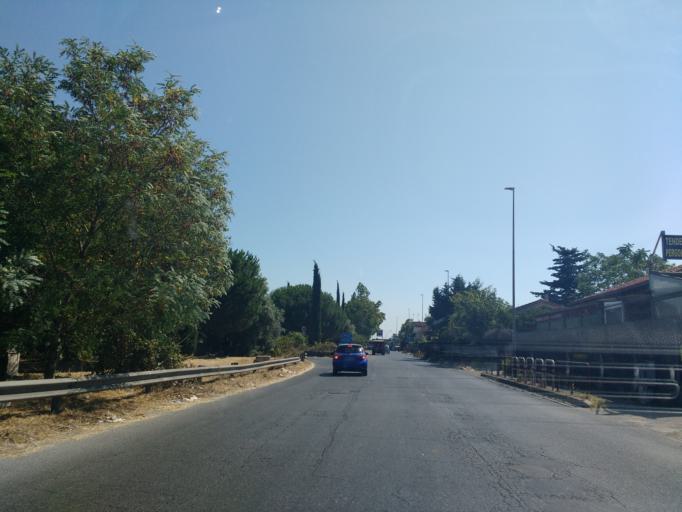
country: IT
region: Latium
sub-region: Citta metropolitana di Roma Capitale
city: Acilia-Castel Fusano-Ostia Antica
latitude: 41.7856
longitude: 12.3659
